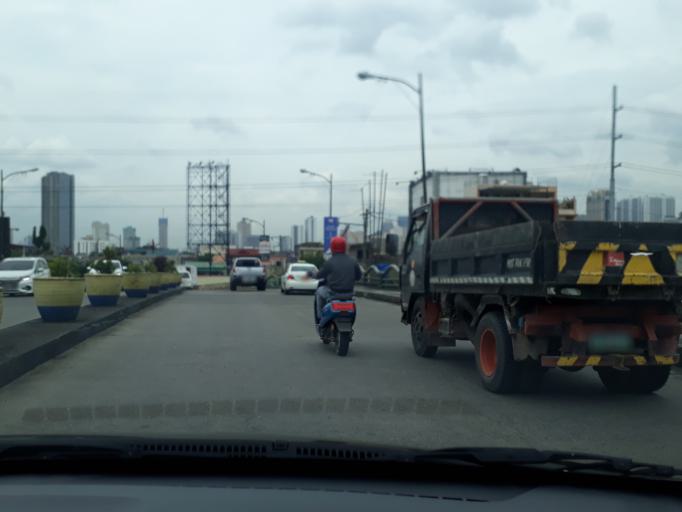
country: PH
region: Metro Manila
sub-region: Mandaluyong
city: Mandaluyong City
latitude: 14.5694
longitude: 121.0317
